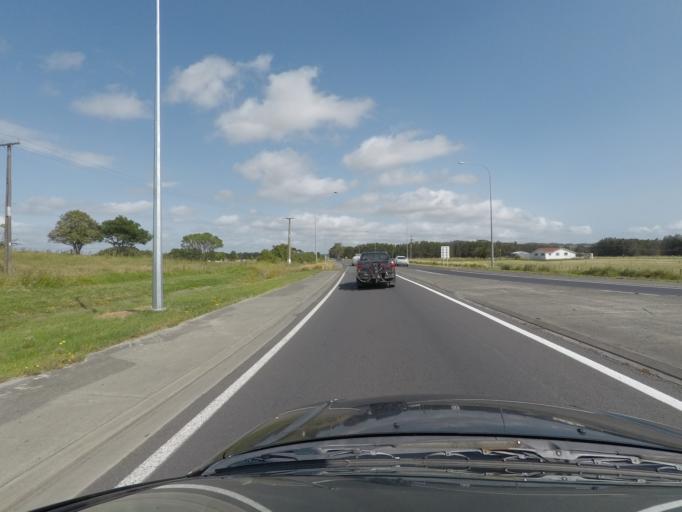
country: NZ
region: Northland
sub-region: Whangarei
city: Ruakaka
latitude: -35.8911
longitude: 174.4322
